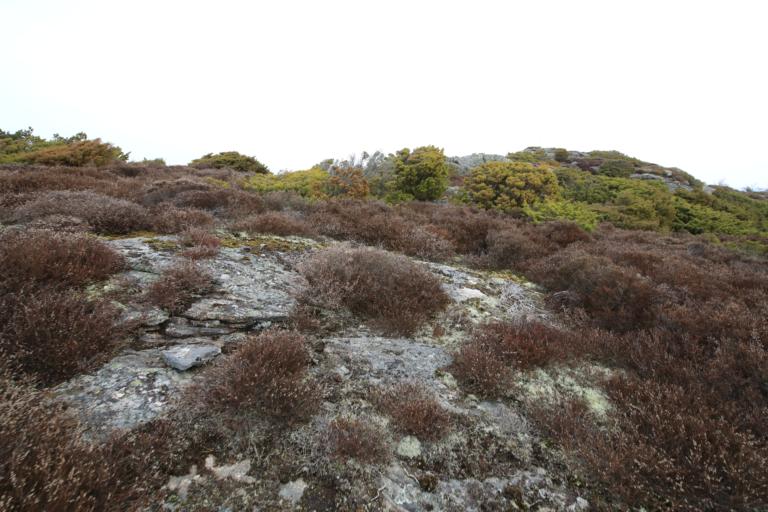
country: SE
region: Halland
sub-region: Kungsbacka Kommun
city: Frillesas
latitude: 57.2484
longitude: 12.1016
